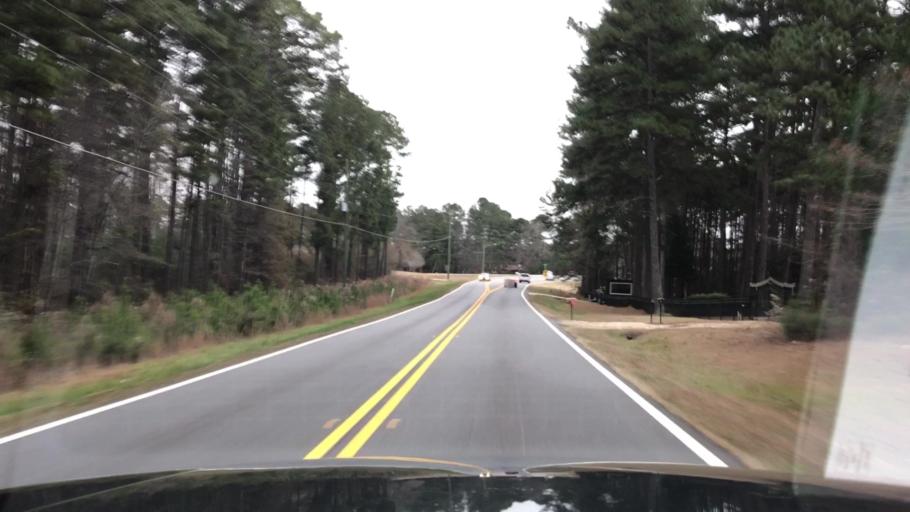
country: US
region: Georgia
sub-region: Walton County
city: Monroe
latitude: 33.8733
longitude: -83.7610
